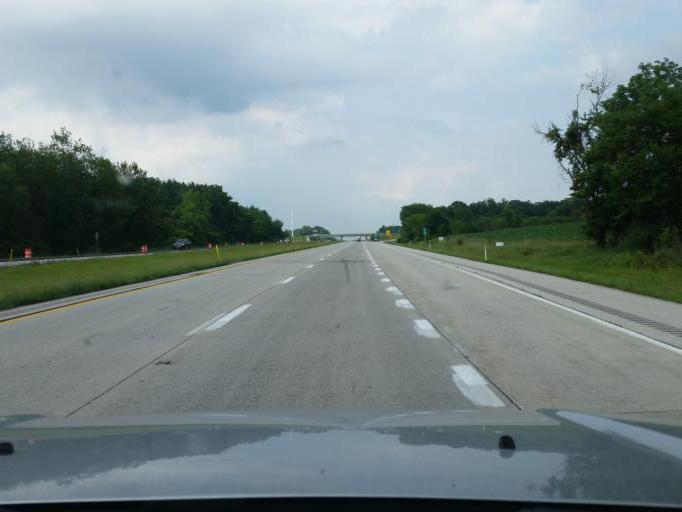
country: US
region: Maryland
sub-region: Frederick County
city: Emmitsburg
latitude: 39.7367
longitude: -77.2953
